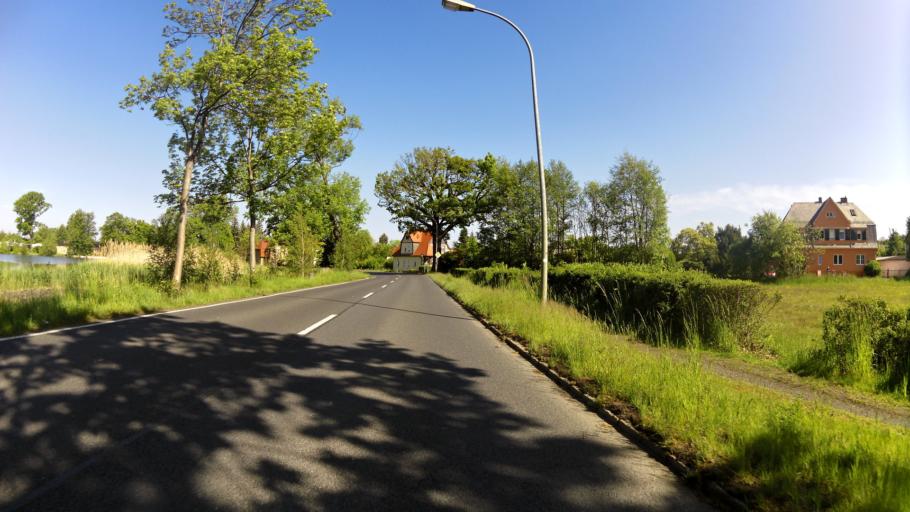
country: DE
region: Saxony
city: Bernsdorf
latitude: 51.3777
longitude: 14.0653
